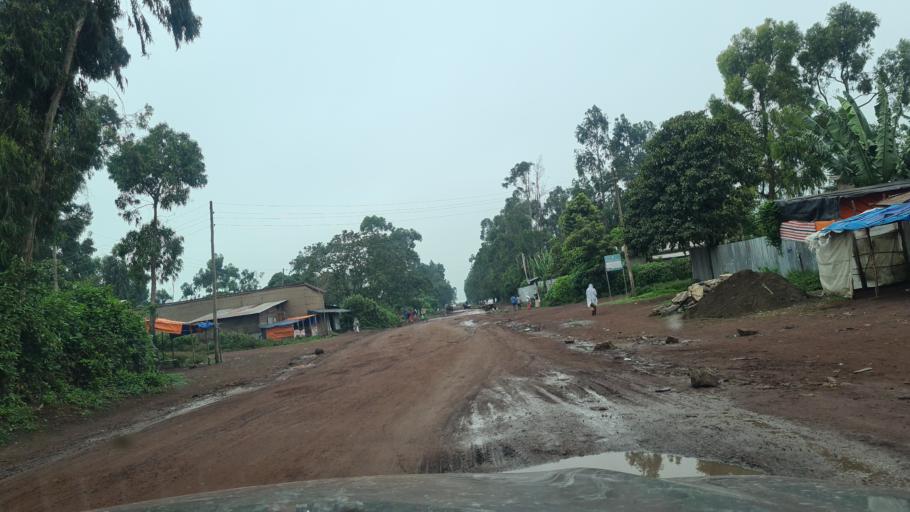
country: ET
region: Oromiya
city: Huruta
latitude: 8.1399
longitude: 39.2391
